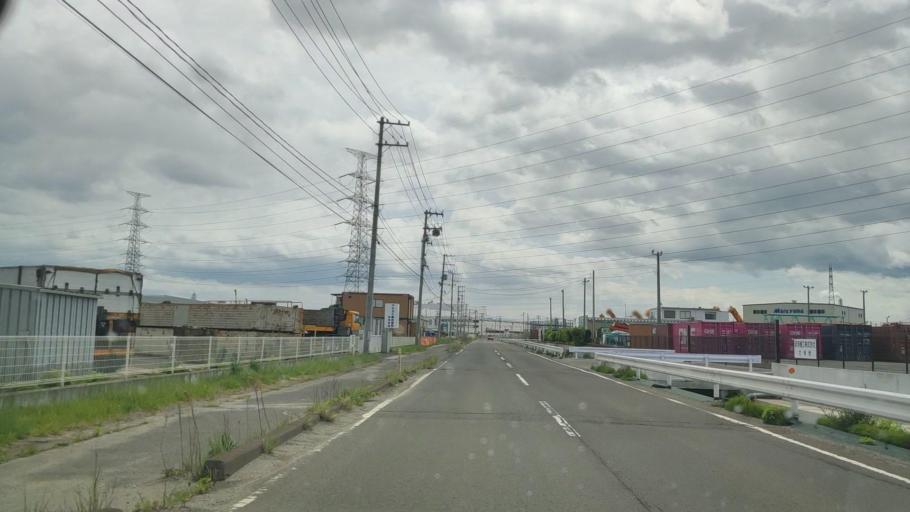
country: JP
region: Miyagi
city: Shiogama
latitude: 38.2799
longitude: 141.0086
